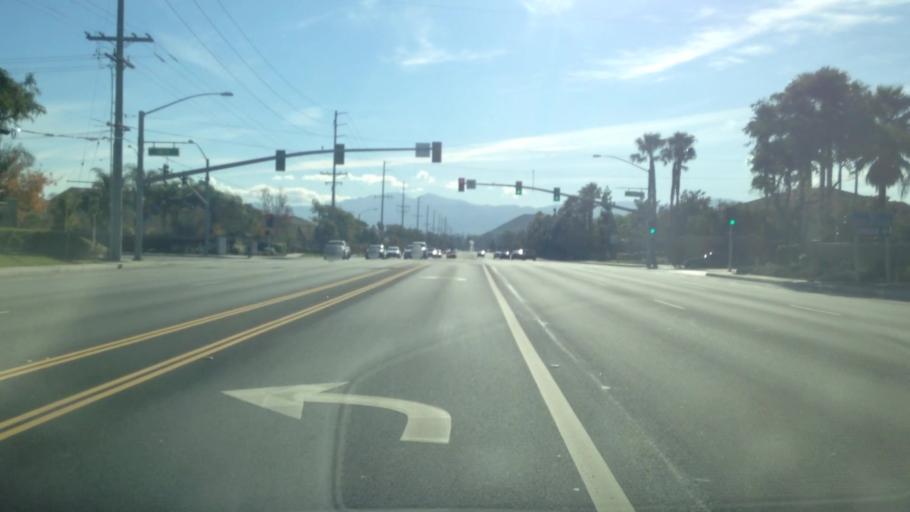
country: US
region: California
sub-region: Riverside County
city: Norco
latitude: 33.9652
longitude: -117.5584
